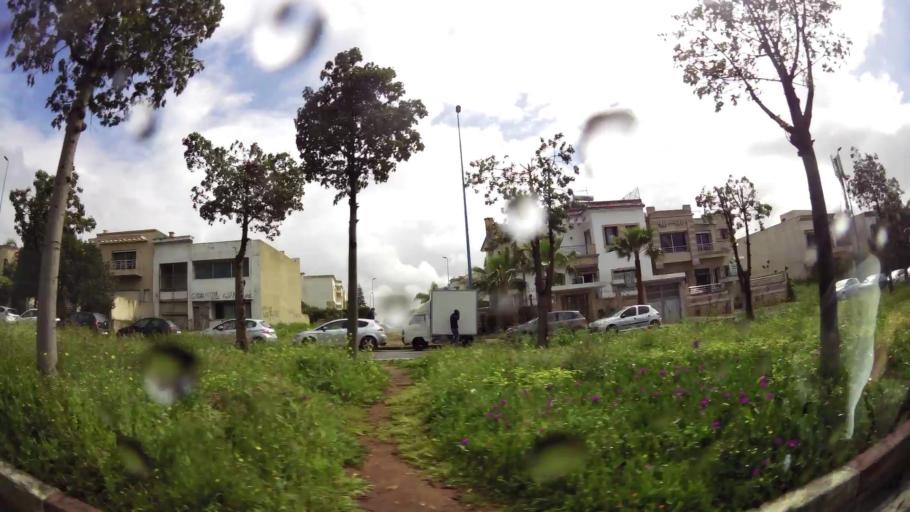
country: MA
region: Grand Casablanca
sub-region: Casablanca
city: Casablanca
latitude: 33.5303
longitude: -7.6428
